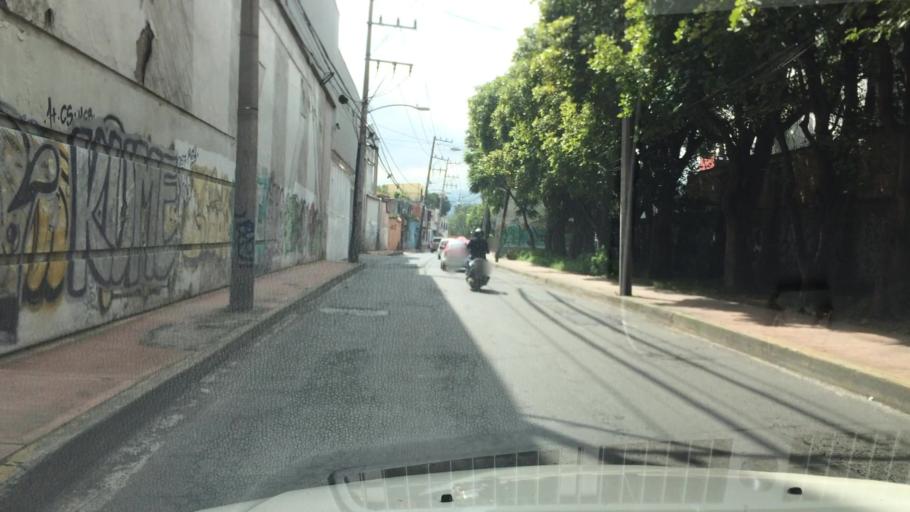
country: MX
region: Mexico City
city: Xochimilco
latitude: 19.2778
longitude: -99.1336
